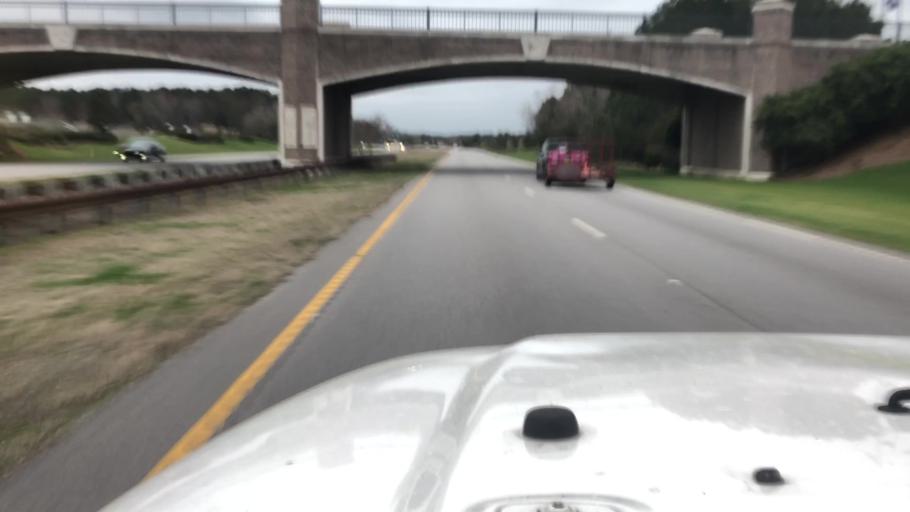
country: US
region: South Carolina
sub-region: Beaufort County
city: Bluffton
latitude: 32.2996
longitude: -80.9499
